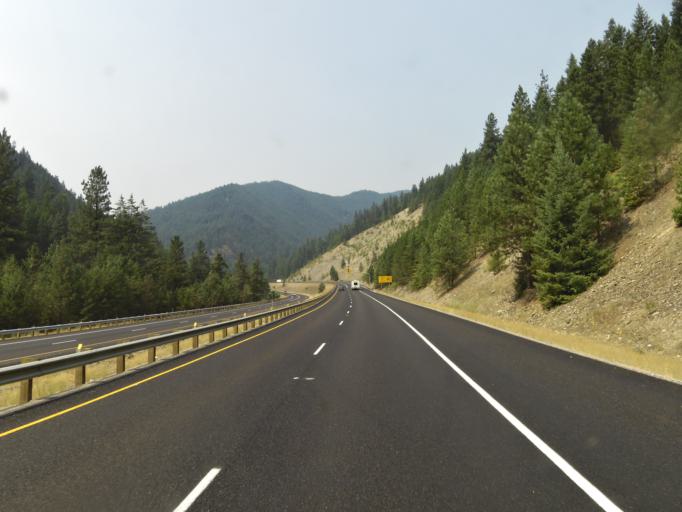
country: US
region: Montana
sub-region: Sanders County
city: Thompson Falls
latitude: 47.3138
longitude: -115.2228
